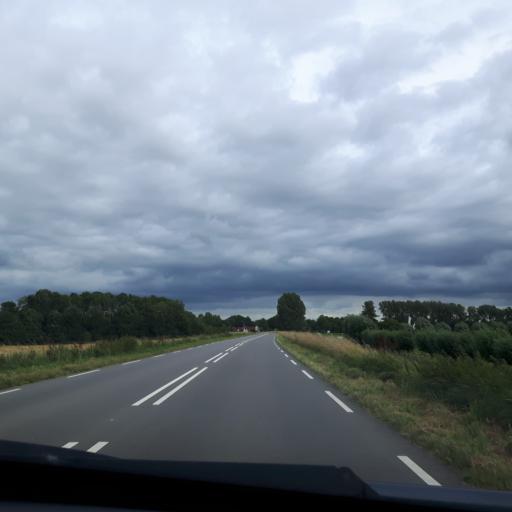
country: NL
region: Zeeland
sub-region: Gemeente Goes
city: Goes
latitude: 51.5601
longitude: 3.8062
